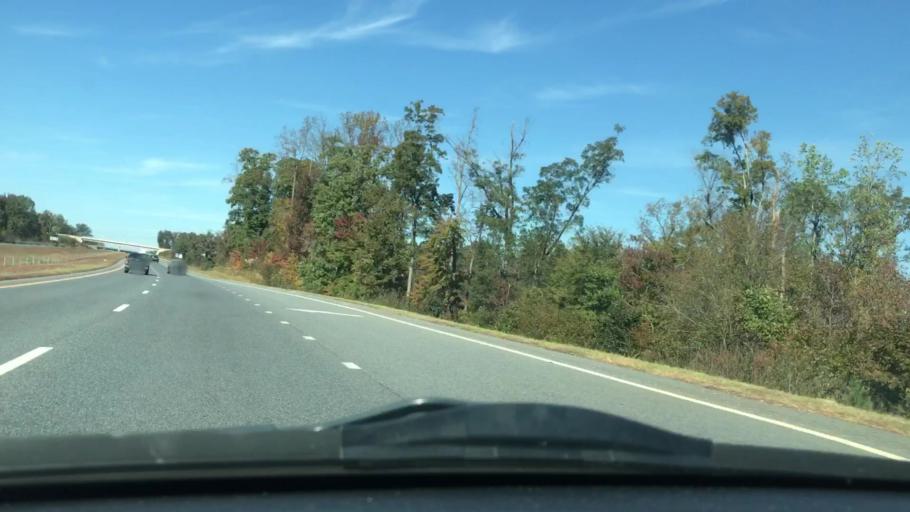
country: US
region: North Carolina
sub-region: Randolph County
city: Randleman
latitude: 35.8266
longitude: -79.8561
